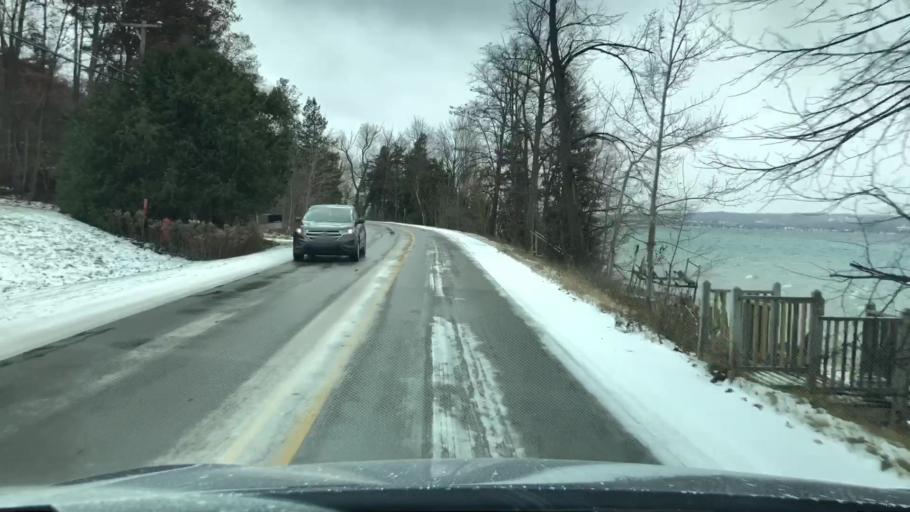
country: US
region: Michigan
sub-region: Grand Traverse County
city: Traverse City
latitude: 44.7991
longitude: -85.5839
